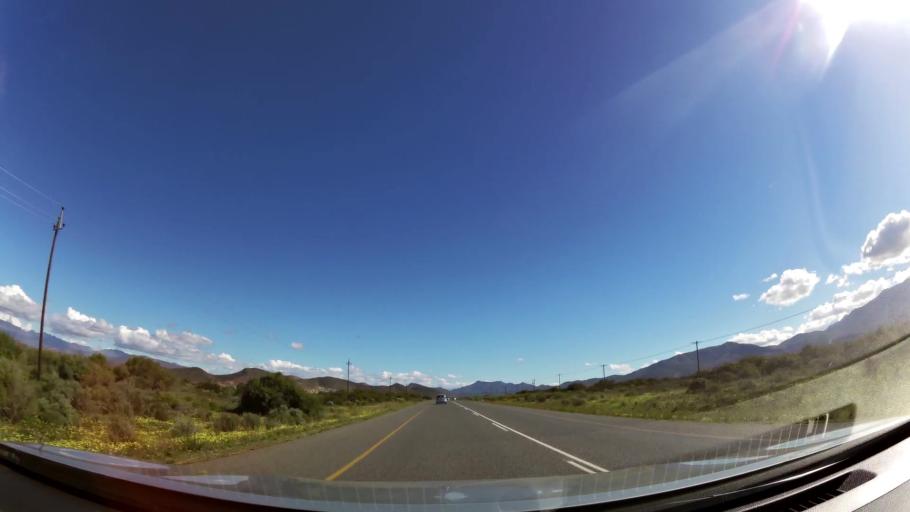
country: ZA
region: Western Cape
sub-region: Cape Winelands District Municipality
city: Ashton
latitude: -33.8144
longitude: 19.9214
